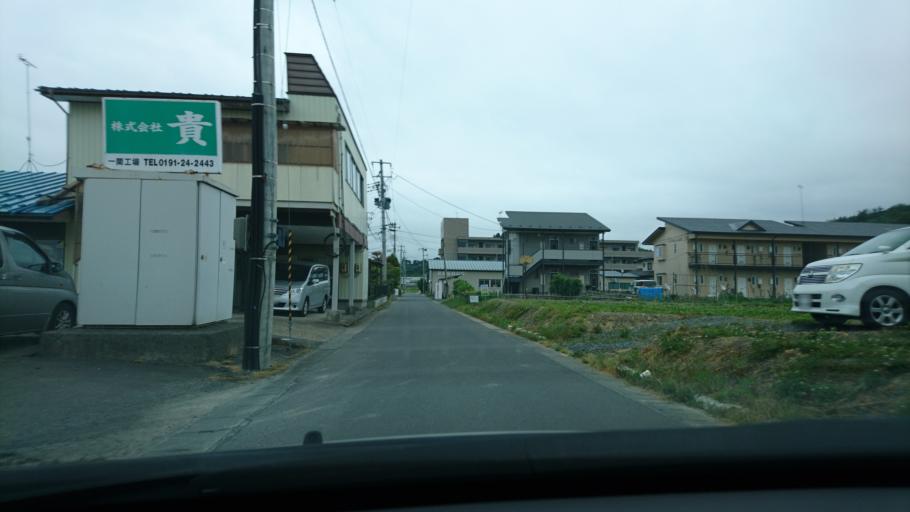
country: JP
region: Iwate
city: Ichinoseki
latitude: 38.9190
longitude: 141.1121
